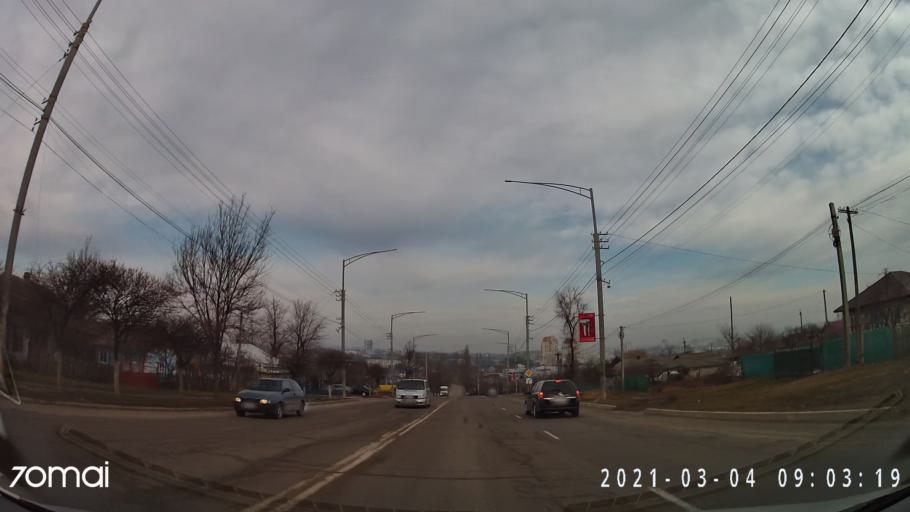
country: MD
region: Balti
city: Balti
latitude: 47.7487
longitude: 27.9454
